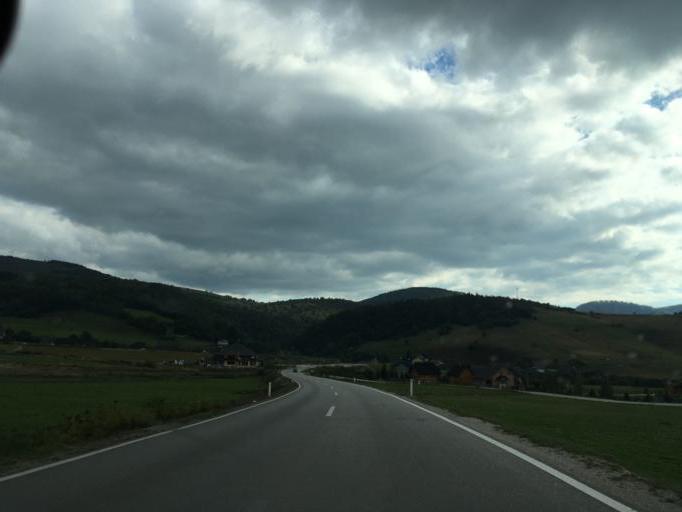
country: BA
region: Federation of Bosnia and Herzegovina
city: Novi Travnik
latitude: 44.1061
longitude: 17.5751
